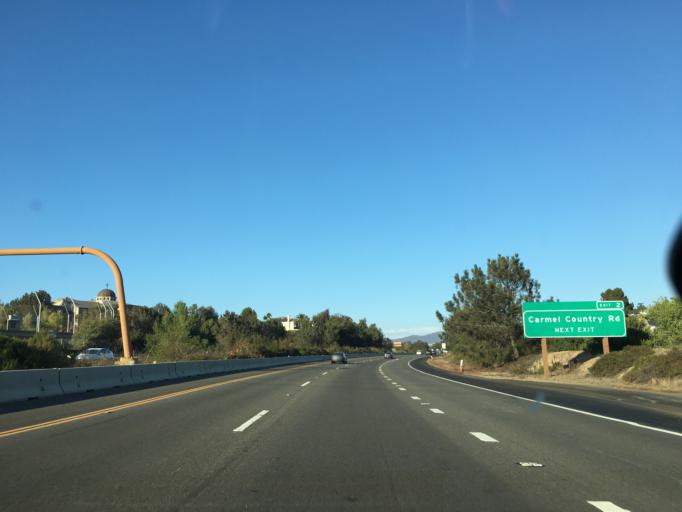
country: US
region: California
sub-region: San Diego County
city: Del Mar
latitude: 32.9400
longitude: -117.2216
